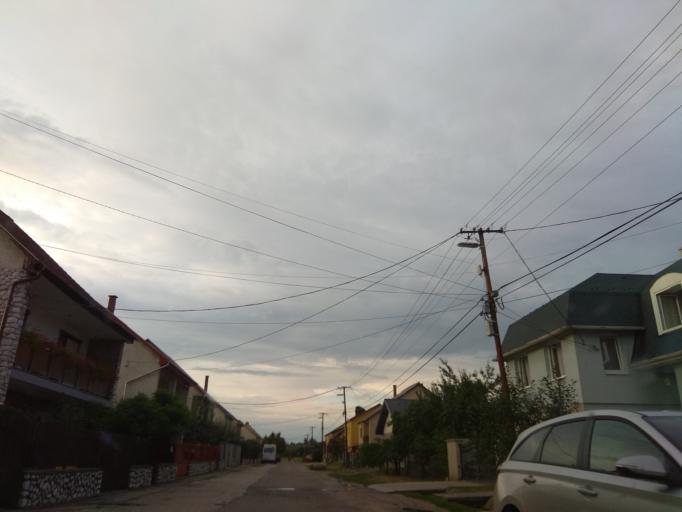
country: HU
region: Borsod-Abauj-Zemplen
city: Miskolc
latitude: 48.0602
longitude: 20.7901
